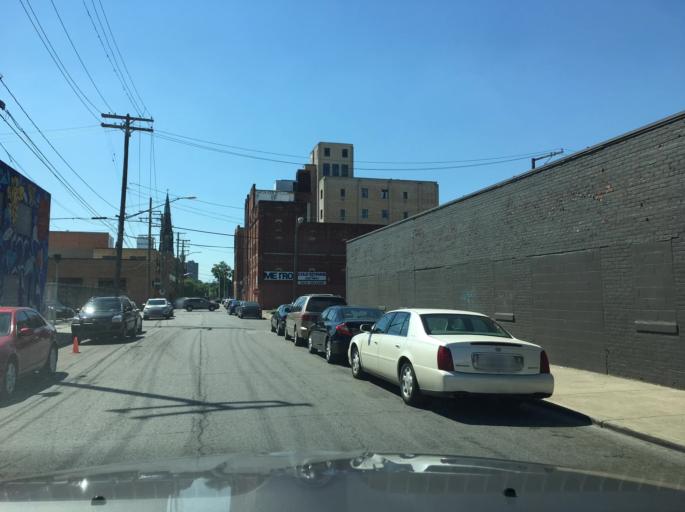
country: US
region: Michigan
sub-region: Wayne County
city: Detroit
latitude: 42.3484
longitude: -83.0380
